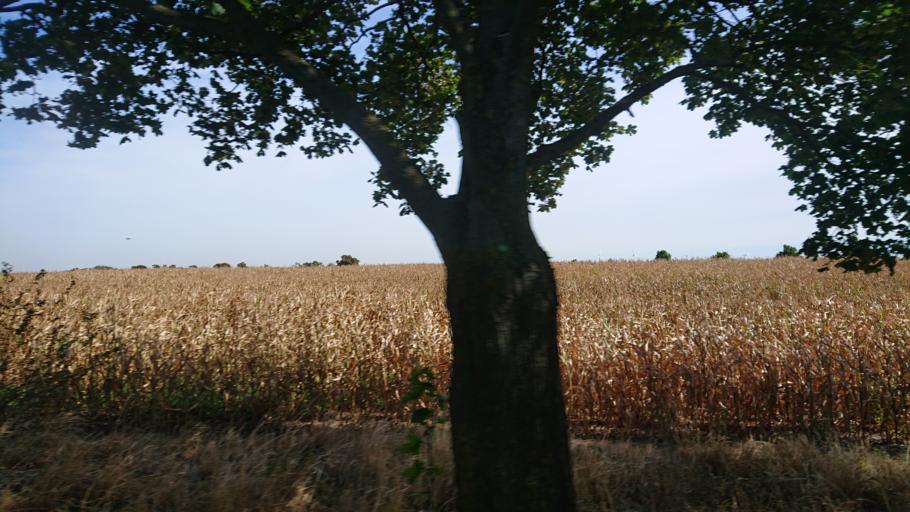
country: DE
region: Berlin
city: Buch
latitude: 52.6322
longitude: 13.5464
